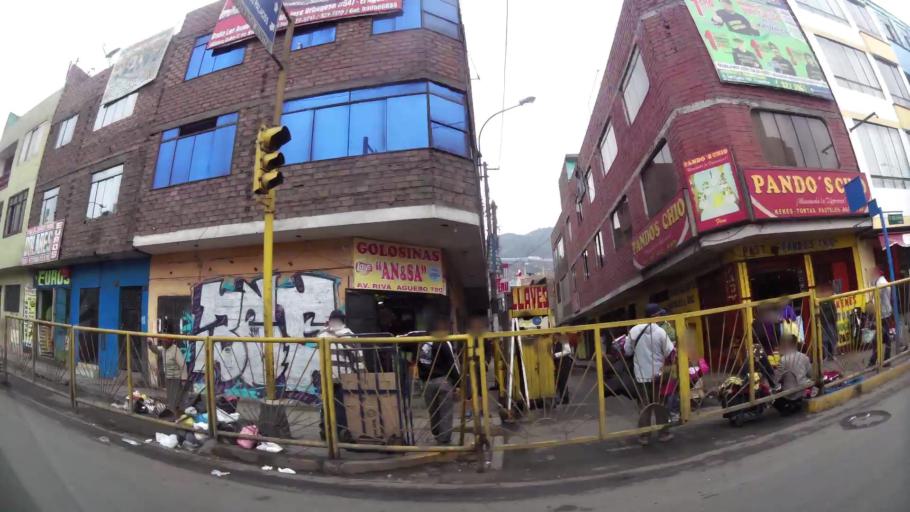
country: PE
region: Lima
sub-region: Lima
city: San Luis
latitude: -12.0527
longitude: -77.0037
